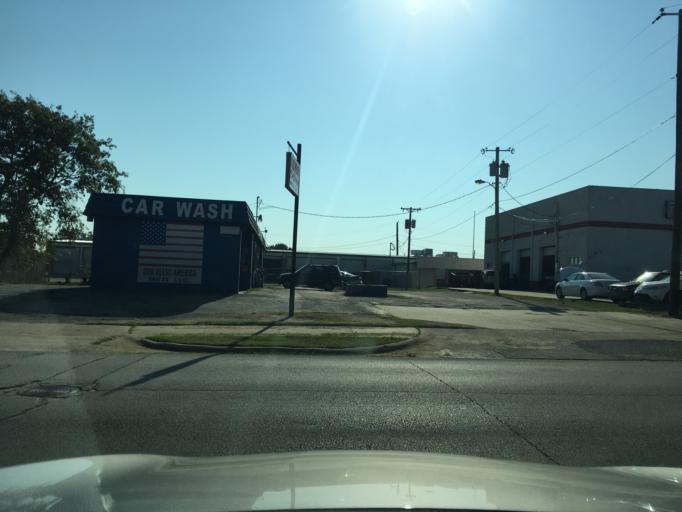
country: US
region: Texas
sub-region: Dallas County
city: Garland
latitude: 32.9458
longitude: -96.6561
